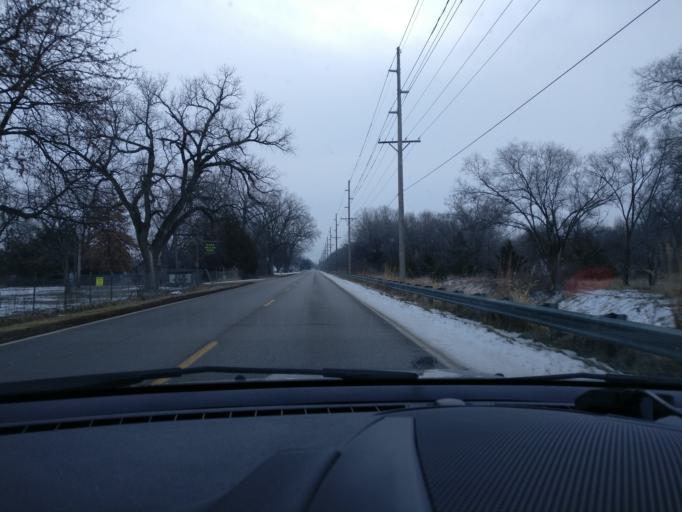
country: US
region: Nebraska
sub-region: Dodge County
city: Fremont
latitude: 41.4415
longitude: -96.5327
